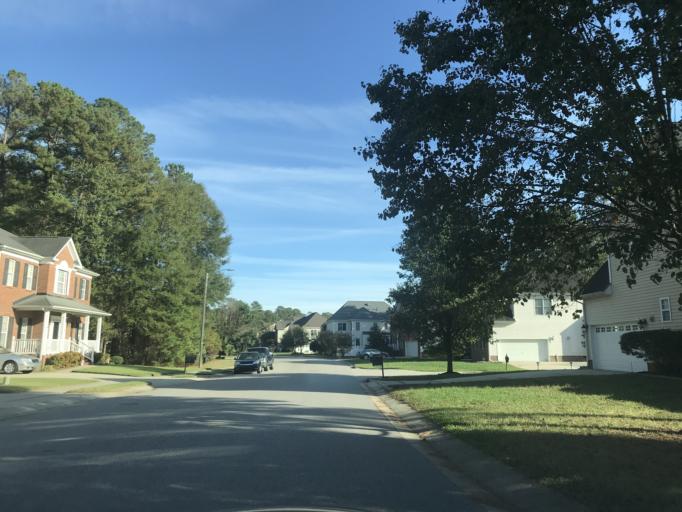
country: US
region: North Carolina
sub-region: Wake County
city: Rolesville
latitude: 35.8922
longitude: -78.5417
